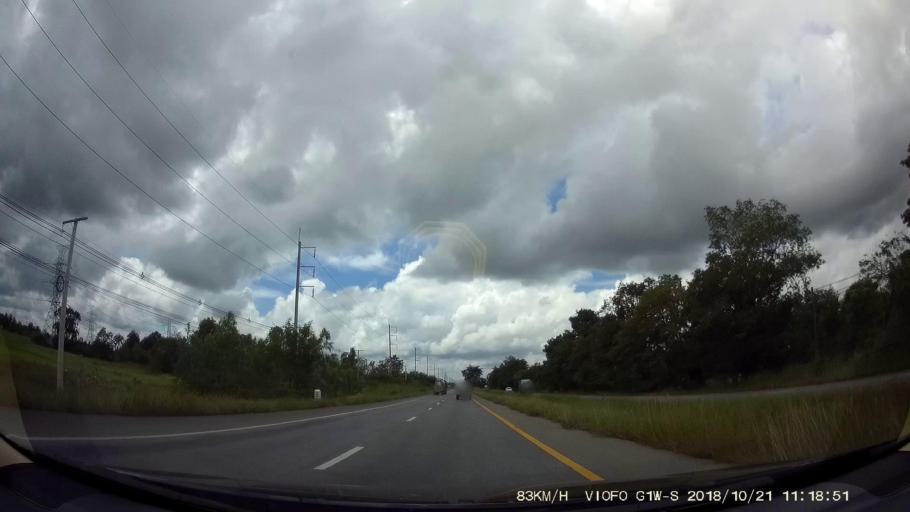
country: TH
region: Chaiyaphum
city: Chaiyaphum
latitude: 15.8742
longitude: 102.0923
